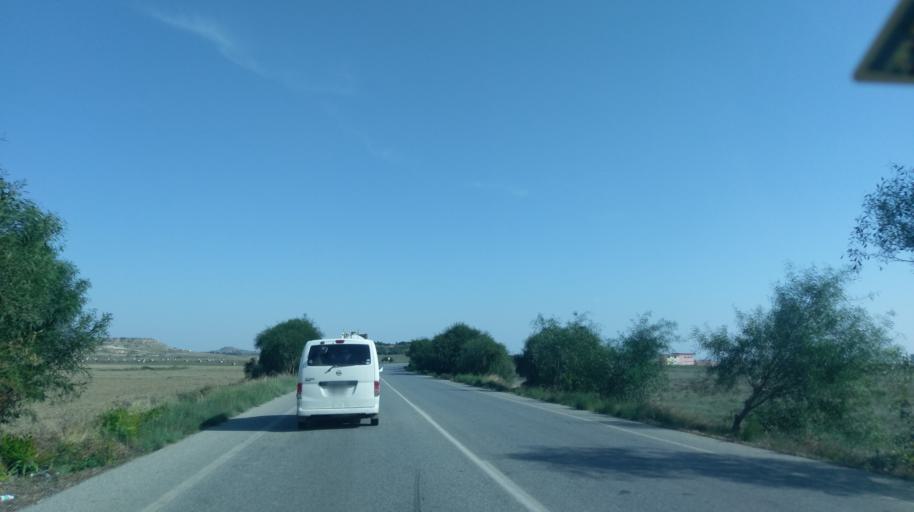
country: CY
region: Ammochostos
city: Trikomo
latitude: 35.2777
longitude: 33.8606
